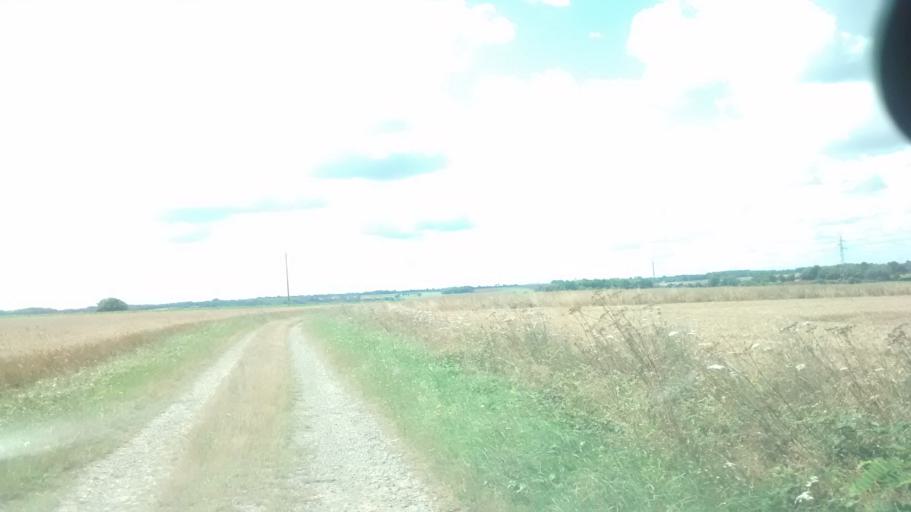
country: FR
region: Brittany
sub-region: Departement d'Ille-et-Vilaine
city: Grand-Fougeray
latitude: 47.7711
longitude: -1.7534
